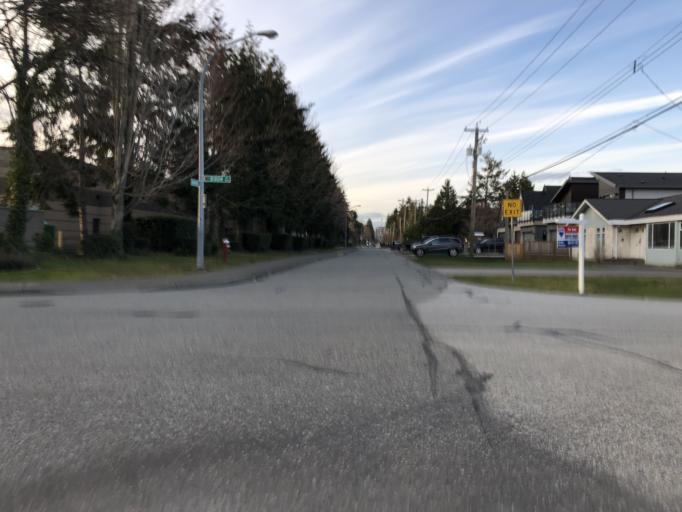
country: CA
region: British Columbia
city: Richmond
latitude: 49.1536
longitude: -123.1225
